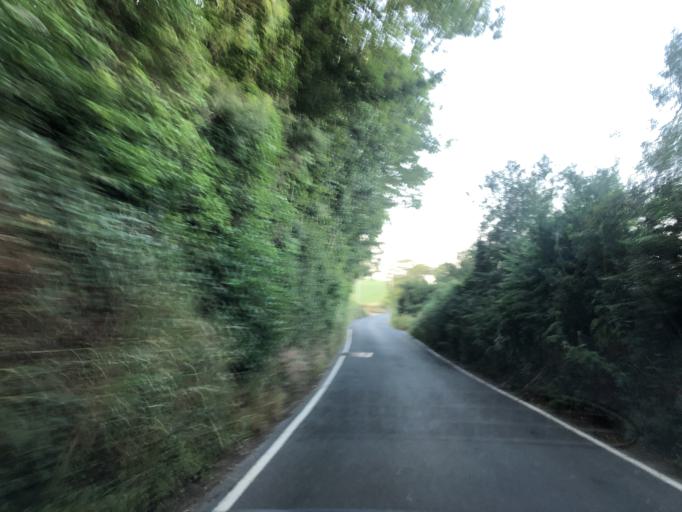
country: GB
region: England
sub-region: Isle of Wight
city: Niton
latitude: 50.5926
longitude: -1.2826
